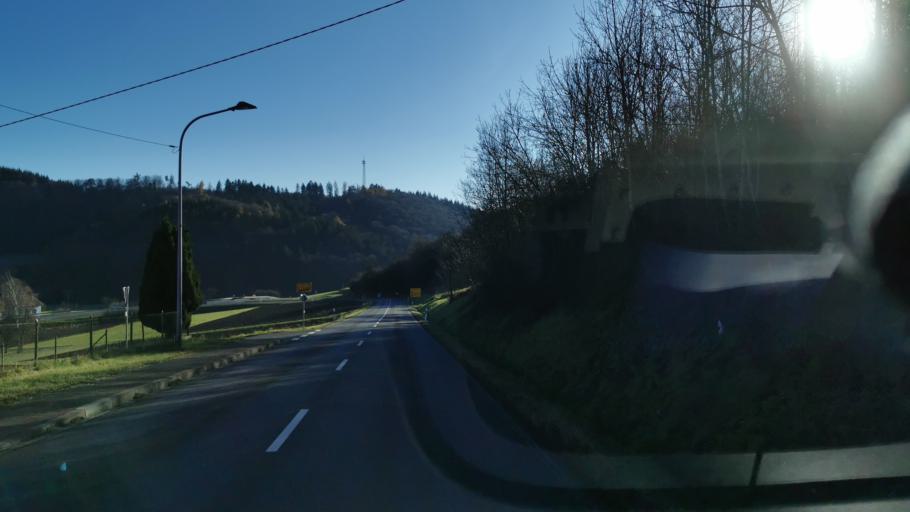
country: DE
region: Rheinland-Pfalz
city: Oberstadtfeld
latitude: 50.1750
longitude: 6.7663
